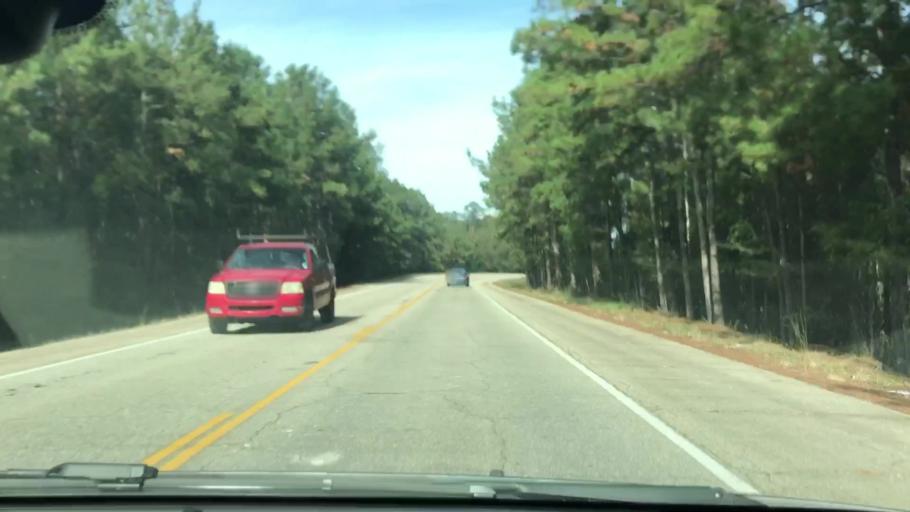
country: US
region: Louisiana
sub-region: Saint Tammany Parish
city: Pearl River
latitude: 30.4724
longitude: -89.8128
